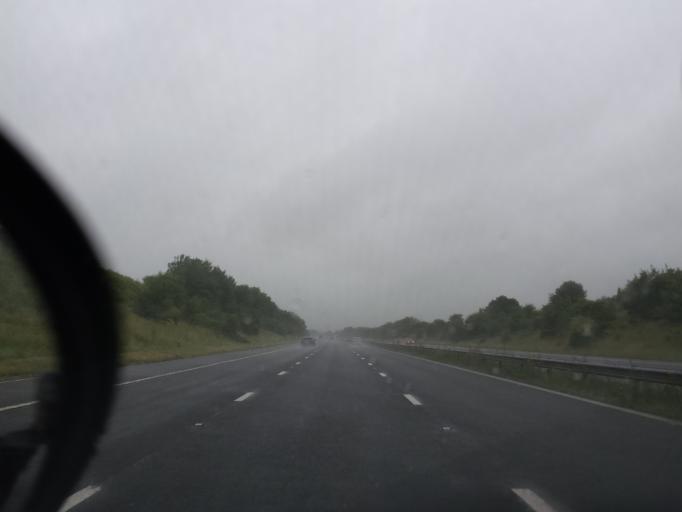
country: GB
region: England
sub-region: Leicestershire
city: Croft
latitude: 52.5857
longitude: -1.2401
